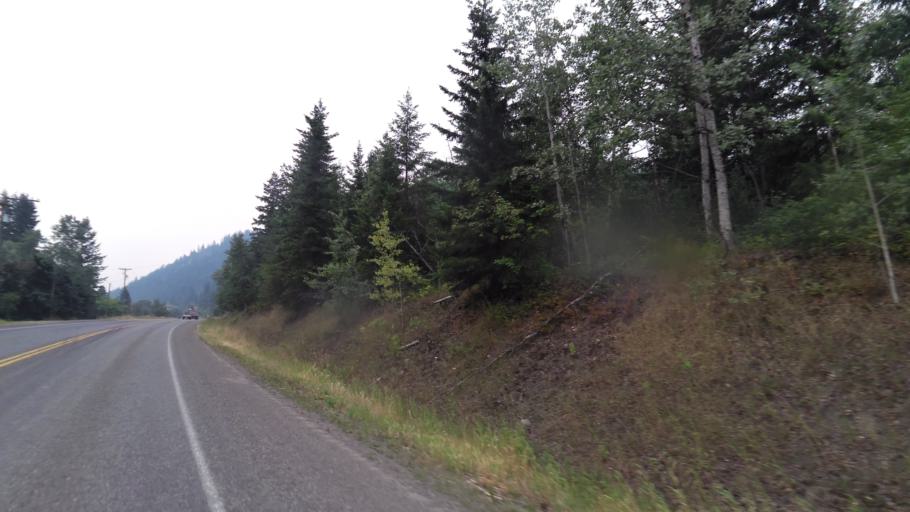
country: CA
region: British Columbia
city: Kamloops
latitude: 51.4078
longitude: -120.2092
